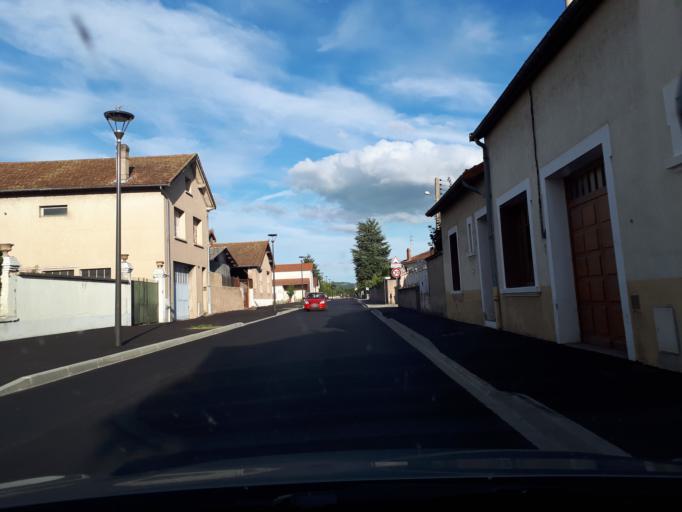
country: FR
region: Rhone-Alpes
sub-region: Departement de la Loire
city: Feurs
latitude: 45.7440
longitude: 4.2335
